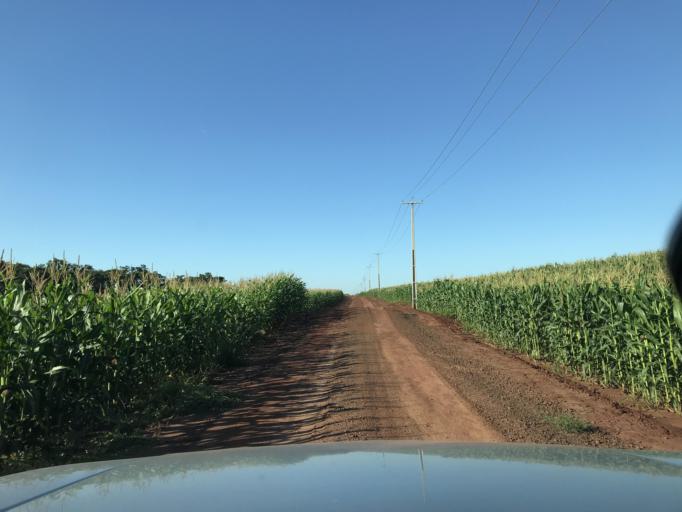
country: BR
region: Parana
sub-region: Palotina
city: Palotina
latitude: -24.2112
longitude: -53.7486
